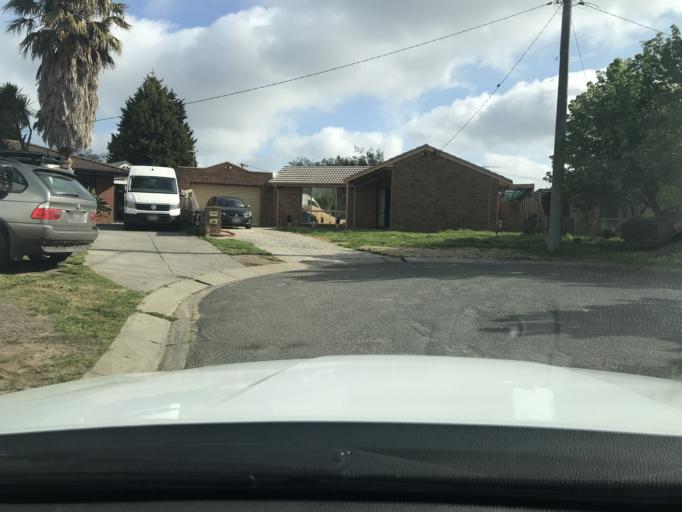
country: AU
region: Victoria
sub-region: Hume
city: Roxburgh Park
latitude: -37.6086
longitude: 144.9303
